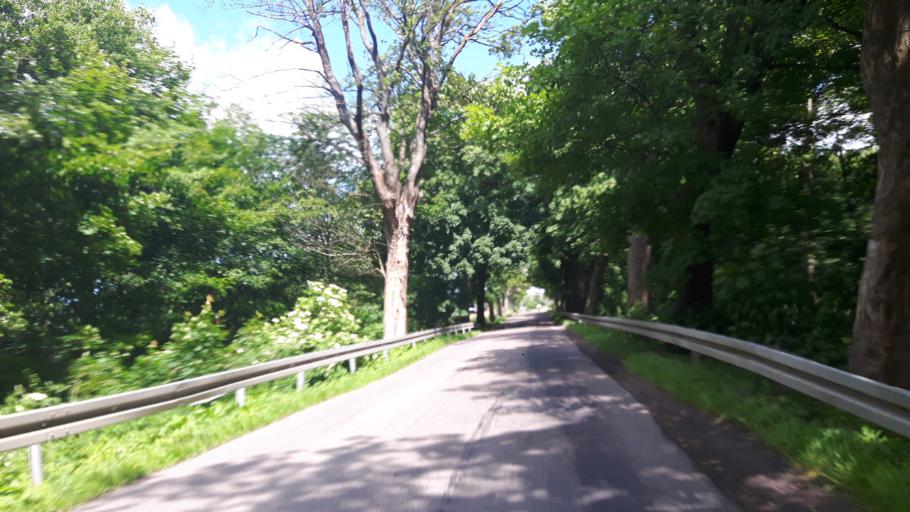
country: PL
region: Pomeranian Voivodeship
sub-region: Powiat slupski
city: Ustka
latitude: 54.5322
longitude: 16.8176
